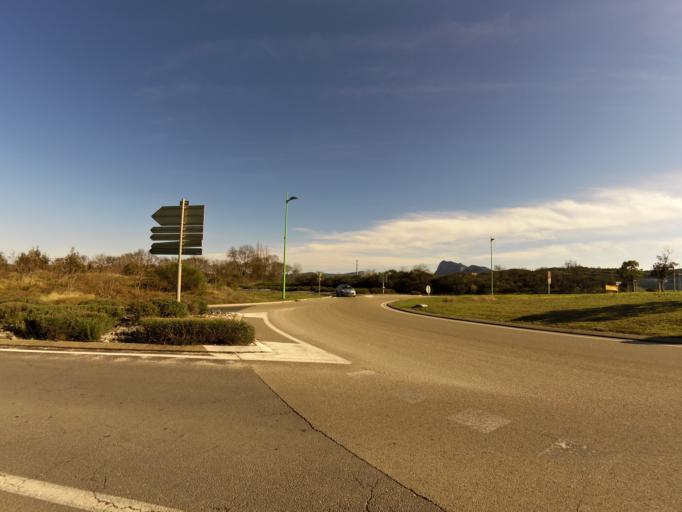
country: FR
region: Languedoc-Roussillon
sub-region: Departement de l'Herault
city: Saint-Martin-de-Londres
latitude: 43.7834
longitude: 3.7358
